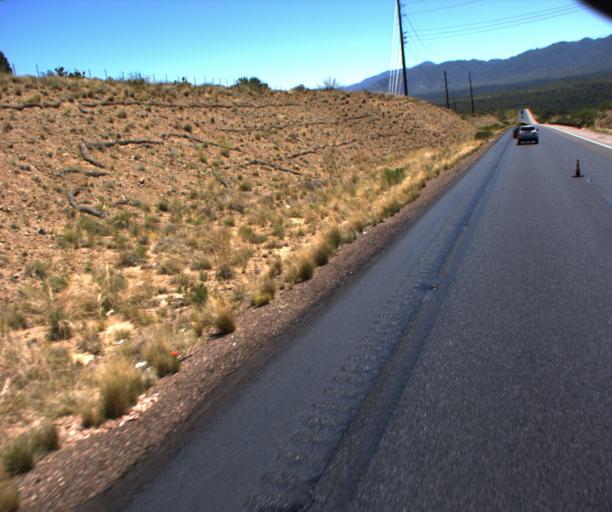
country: US
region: Arizona
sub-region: Gila County
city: Payson
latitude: 34.1369
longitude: -111.3527
